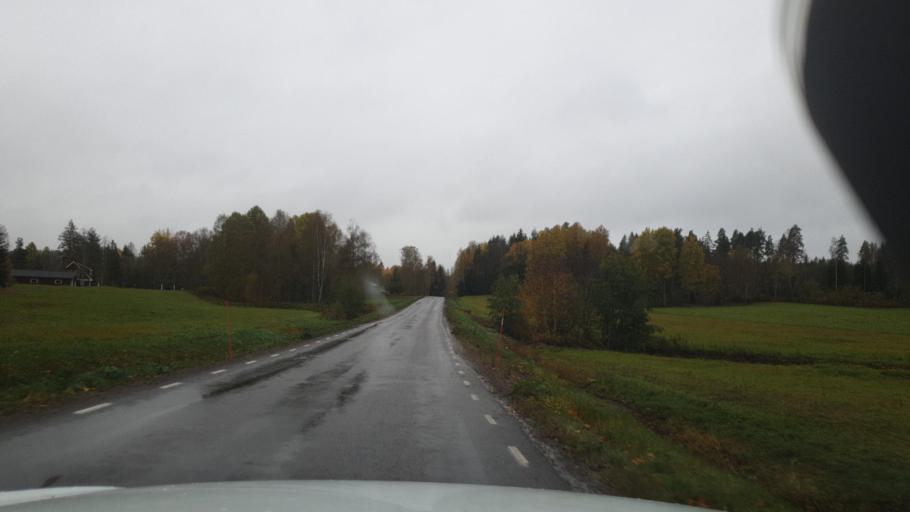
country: SE
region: Vaermland
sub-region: Eda Kommun
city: Charlottenberg
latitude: 59.8044
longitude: 12.1525
